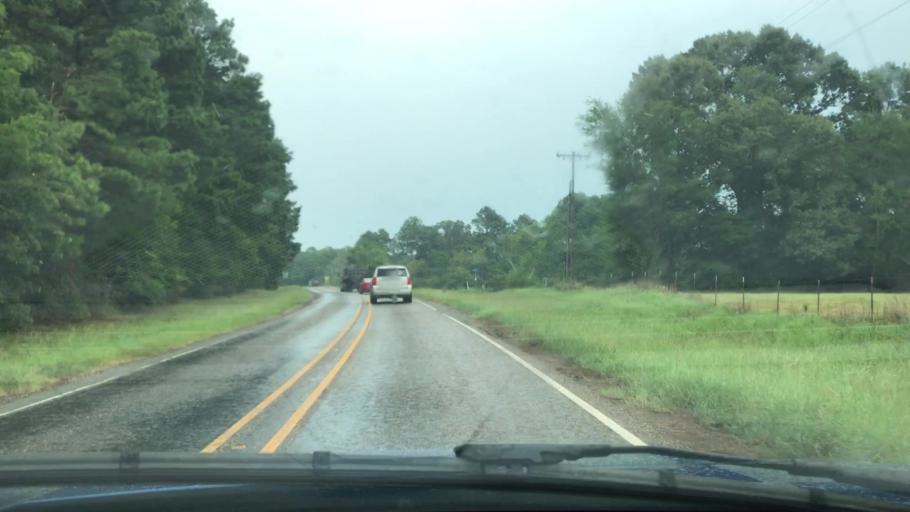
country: US
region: Texas
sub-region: Harrison County
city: Waskom
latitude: 32.4833
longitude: -94.1148
